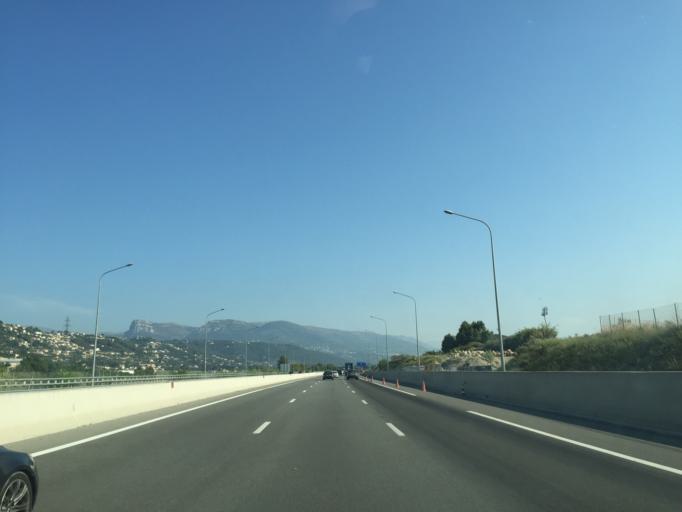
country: FR
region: Provence-Alpes-Cote d'Azur
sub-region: Departement des Alpes-Maritimes
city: Saint-Laurent-du-Var
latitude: 43.6863
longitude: 7.1911
